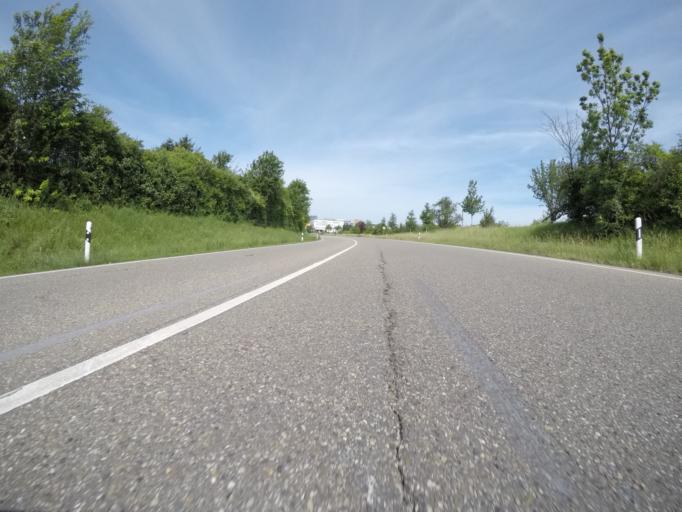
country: DE
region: Baden-Wuerttemberg
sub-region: Regierungsbezirk Stuttgart
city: Korntal
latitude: 48.8166
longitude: 9.1009
